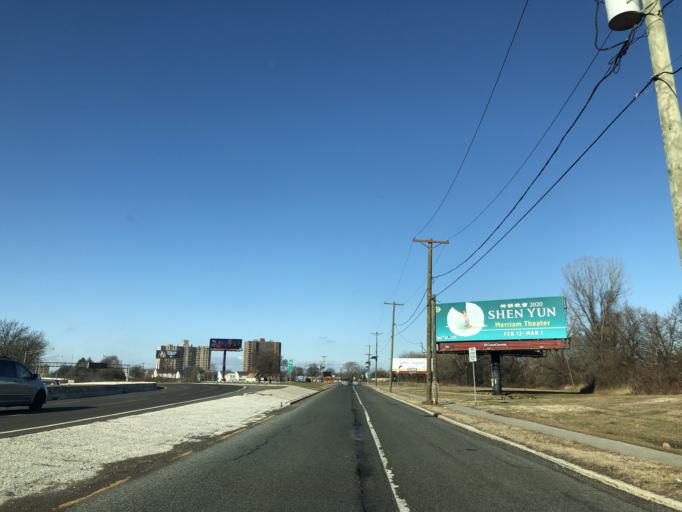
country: US
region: New Jersey
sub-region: Camden County
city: Camden
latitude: 39.9443
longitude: -75.1070
